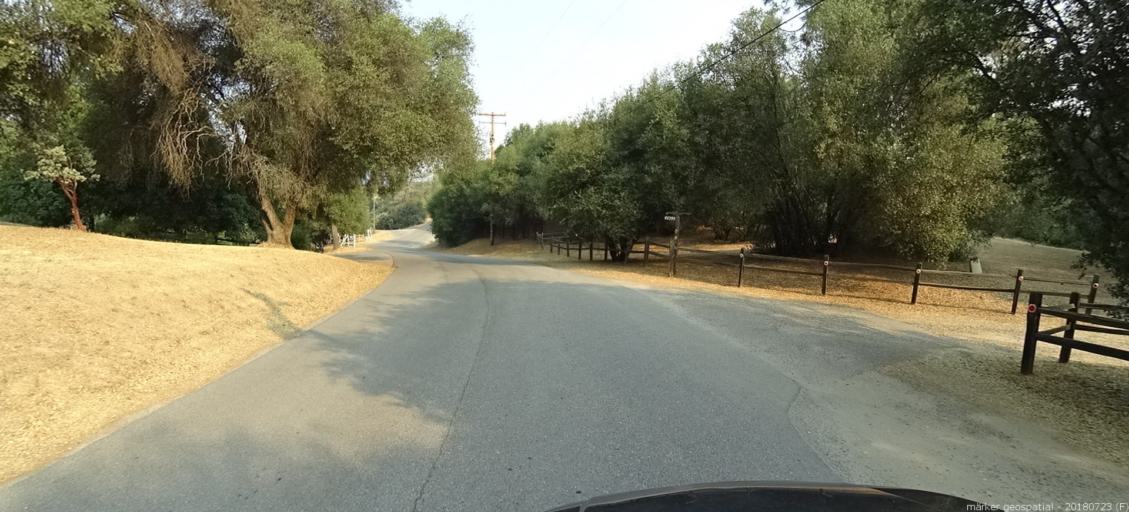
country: US
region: California
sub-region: Madera County
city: Ahwahnee
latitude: 37.3649
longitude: -119.7306
